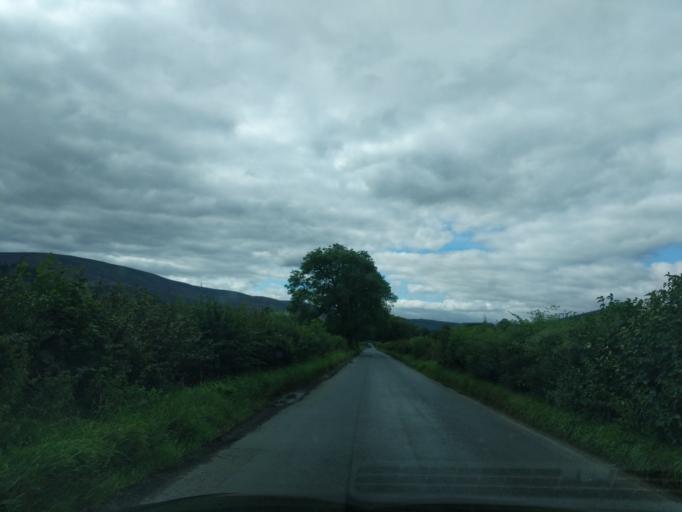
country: GB
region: Scotland
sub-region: The Scottish Borders
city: Peebles
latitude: 55.6226
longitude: -3.3009
